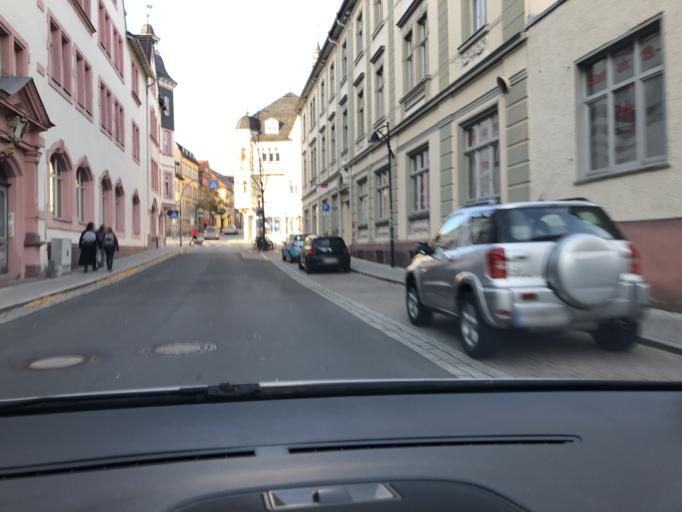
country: DE
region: Thuringia
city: Ilmenau
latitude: 50.6845
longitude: 10.9148
